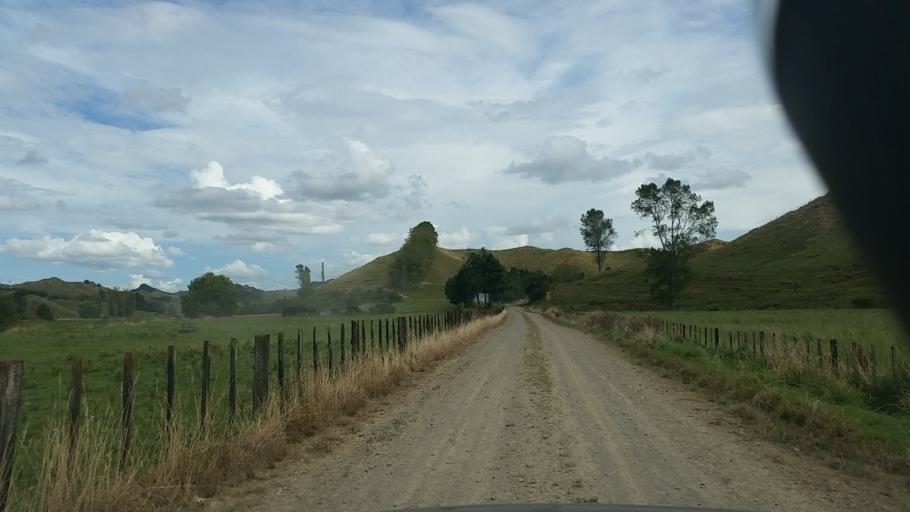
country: NZ
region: Taranaki
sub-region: South Taranaki District
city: Eltham
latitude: -39.2833
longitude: 174.4972
